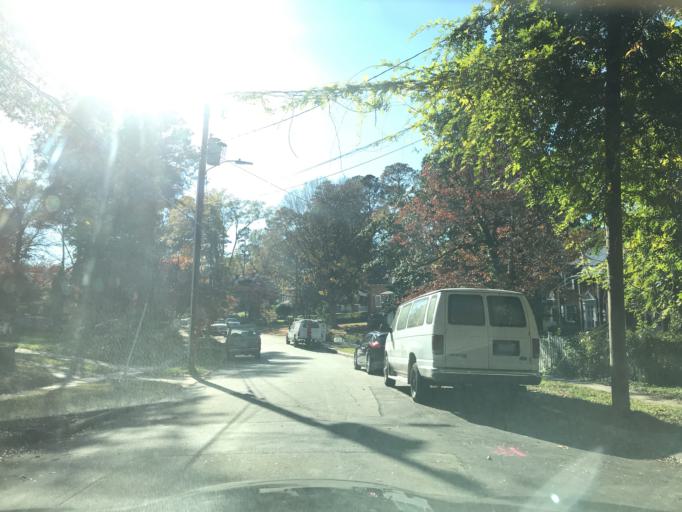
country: US
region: North Carolina
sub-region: Wake County
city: Raleigh
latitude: 35.7983
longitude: -78.6301
